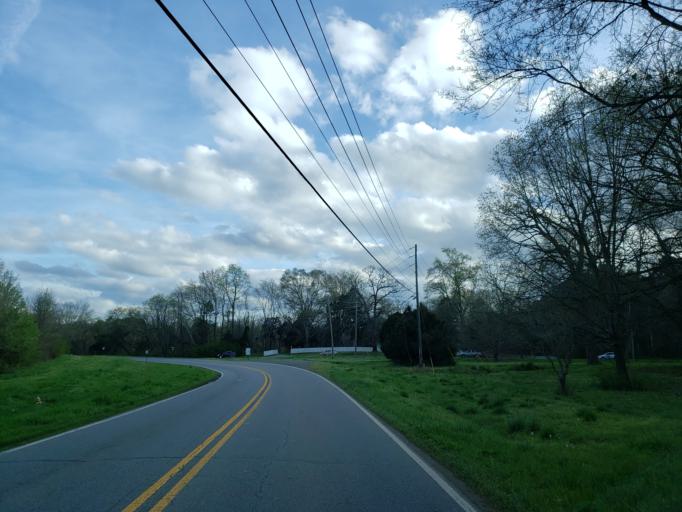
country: US
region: Georgia
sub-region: Bartow County
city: Cartersville
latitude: 34.2234
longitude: -84.8047
